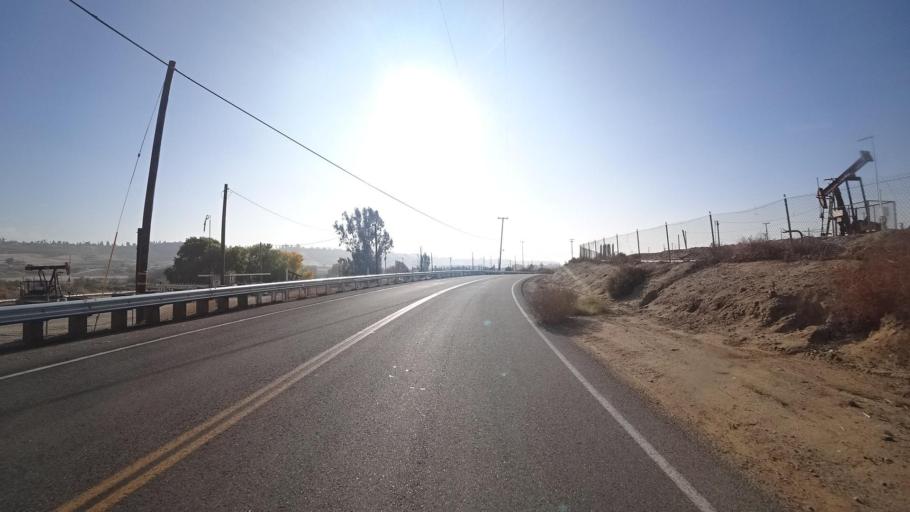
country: US
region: California
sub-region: Kern County
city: Oildale
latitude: 35.4283
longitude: -118.9544
